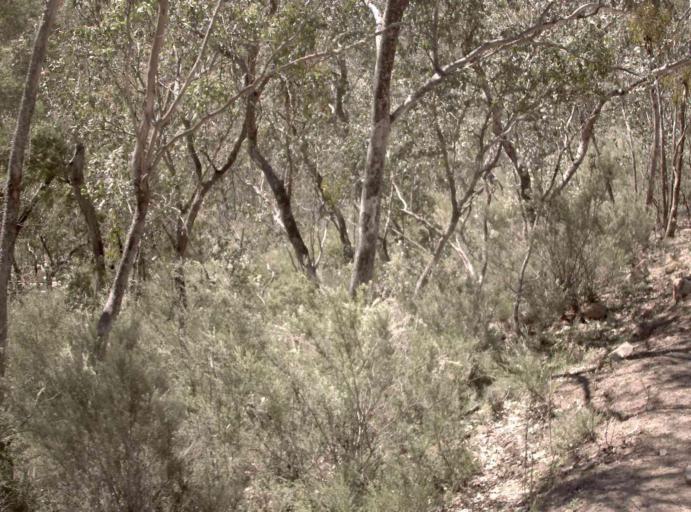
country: AU
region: New South Wales
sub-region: Snowy River
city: Jindabyne
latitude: -37.0644
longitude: 148.5158
